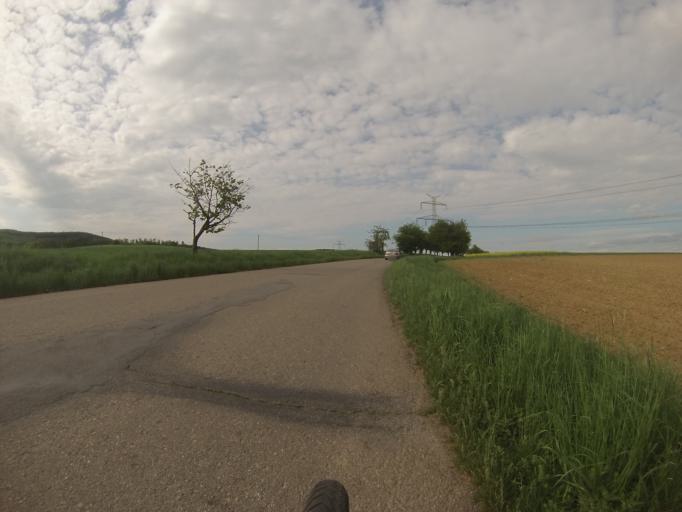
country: CZ
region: South Moravian
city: Veverska Bityska
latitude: 49.2866
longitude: 16.4449
